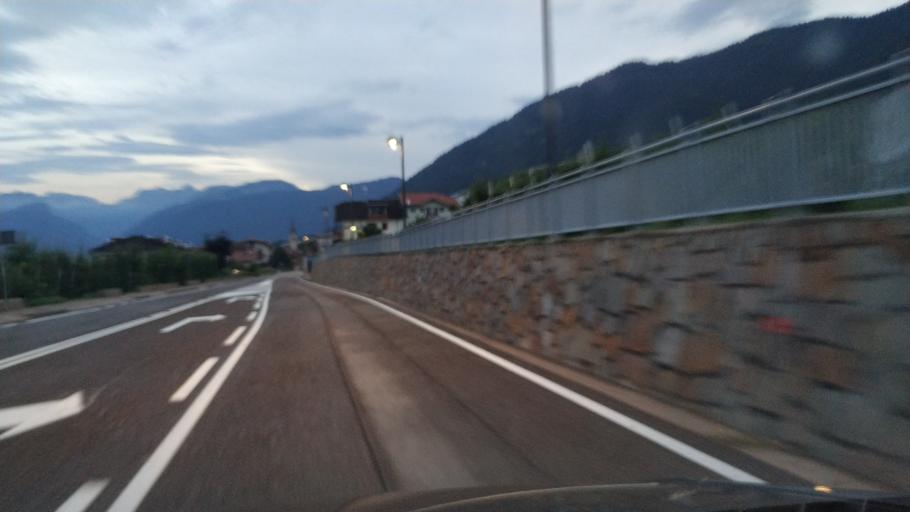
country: IT
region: Trentino-Alto Adige
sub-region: Provincia di Trento
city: Cloz
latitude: 46.4242
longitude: 11.0935
